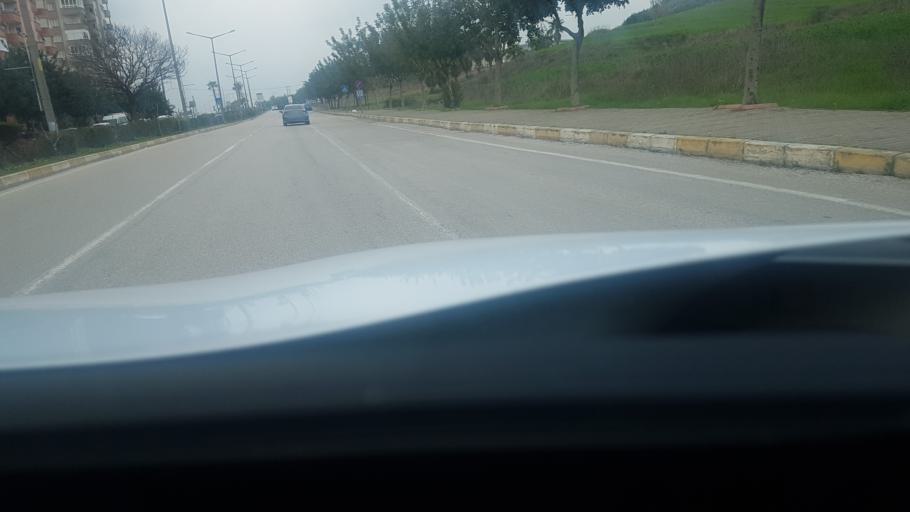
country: TR
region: Adana
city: Seyhan
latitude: 37.0542
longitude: 35.2502
